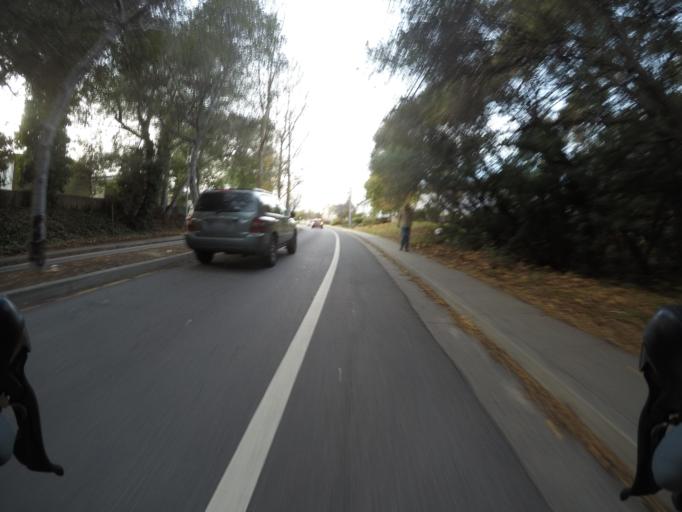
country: US
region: California
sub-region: Santa Cruz County
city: Live Oak
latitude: 36.9747
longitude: -121.9754
